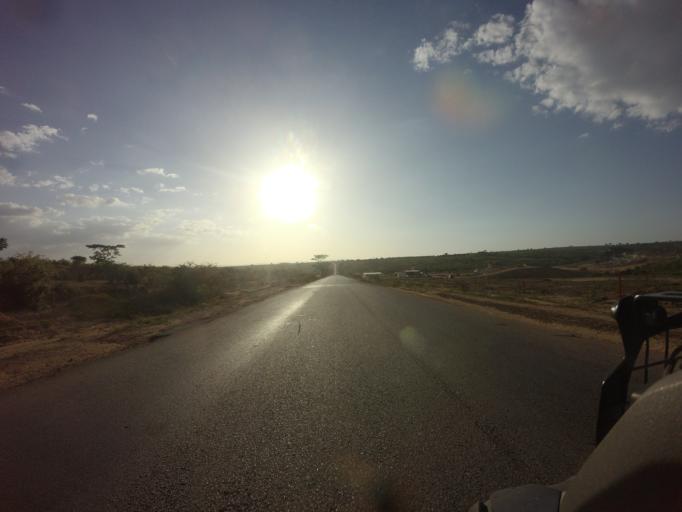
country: AO
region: Huila
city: Lubango
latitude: -14.7852
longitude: 13.7284
